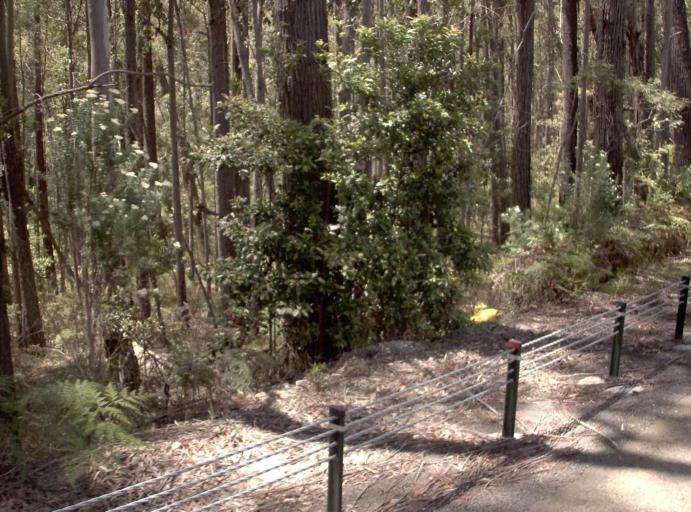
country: AU
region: Victoria
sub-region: East Gippsland
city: Lakes Entrance
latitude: -37.6585
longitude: 148.8065
